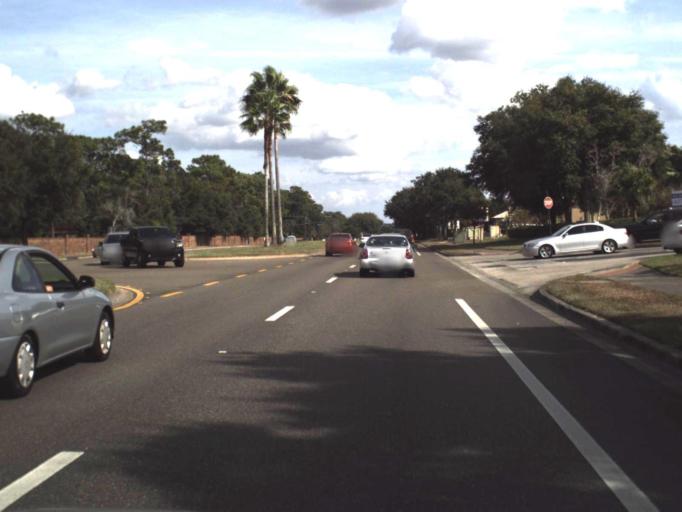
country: US
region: Florida
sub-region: Seminole County
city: Heathrow
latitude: 28.7560
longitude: -81.3455
